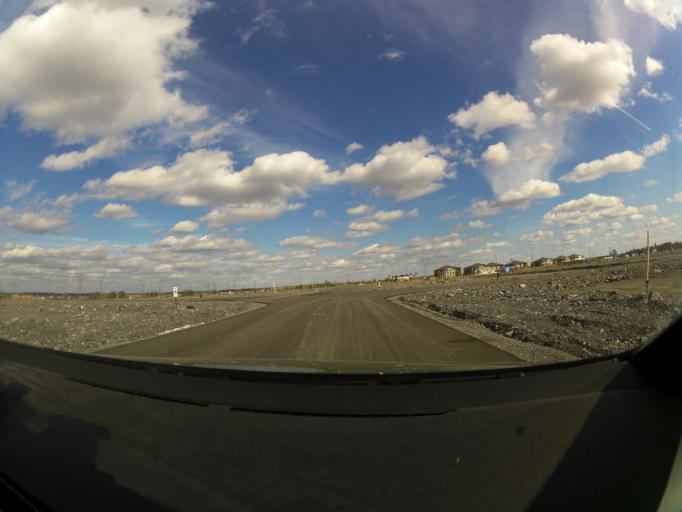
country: CA
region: Ontario
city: Bells Corners
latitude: 45.2695
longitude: -75.8959
